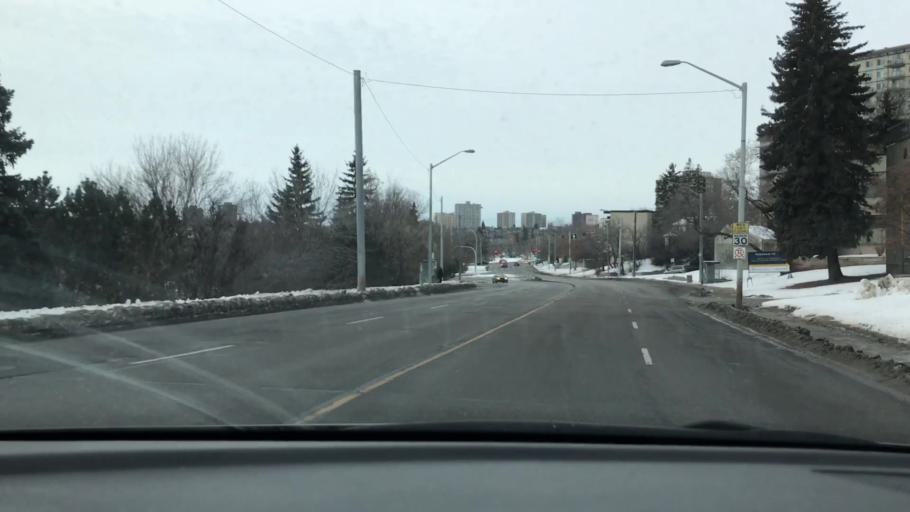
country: CA
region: Alberta
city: Edmonton
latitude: 53.5361
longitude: -113.4959
